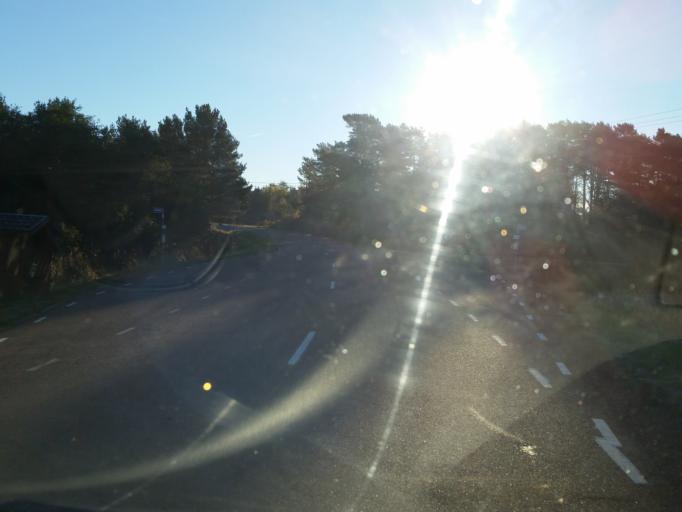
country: AX
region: Alands skaergard
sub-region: Vardoe
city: Vardoe
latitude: 60.2308
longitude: 20.3789
